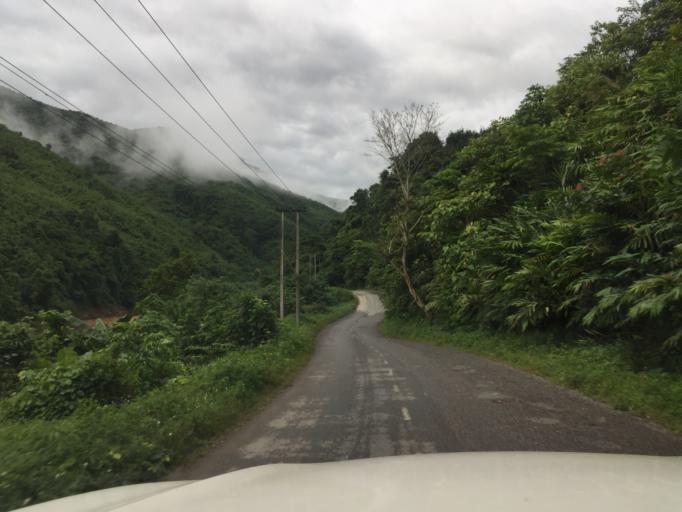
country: LA
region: Oudomxai
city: Muang La
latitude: 21.0454
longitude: 102.2410
